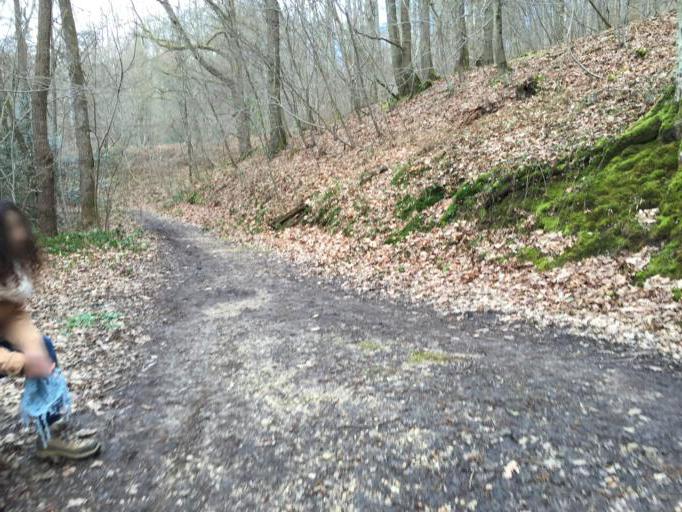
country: FR
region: Ile-de-France
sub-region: Departement des Yvelines
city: Cernay-la-Ville
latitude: 48.6805
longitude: 1.9497
